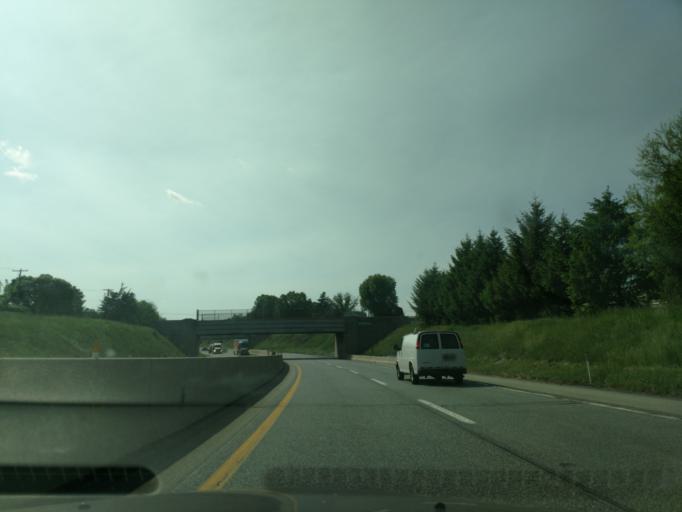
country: US
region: Pennsylvania
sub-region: Lancaster County
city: Denver
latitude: 40.2390
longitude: -76.1321
